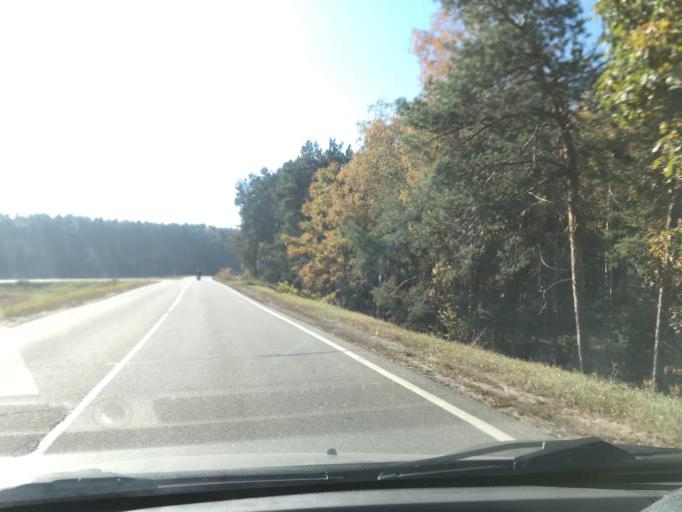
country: BY
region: Gomel
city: Gomel
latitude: 52.3889
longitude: 30.8252
